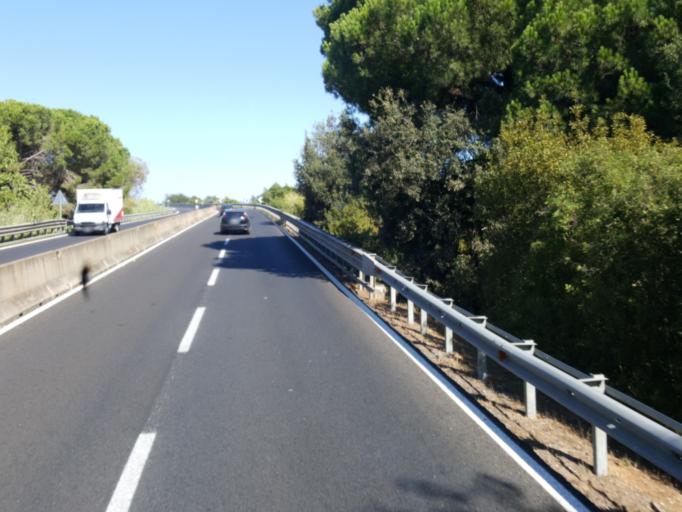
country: IT
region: Tuscany
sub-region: Provincia di Grosseto
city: Orbetello Scalo
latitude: 42.4760
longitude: 11.2322
